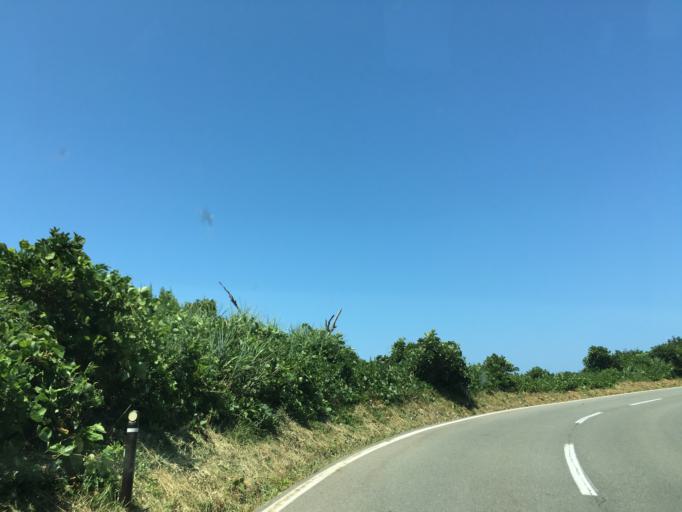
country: JP
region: Akita
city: Tenno
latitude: 39.9298
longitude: 139.7110
